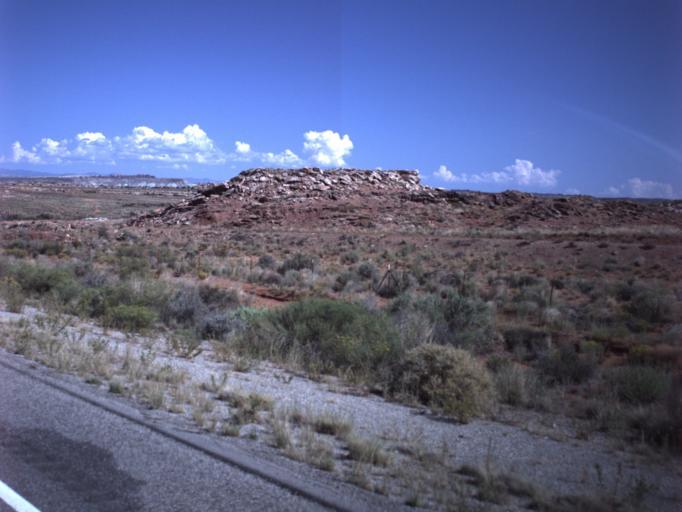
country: US
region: Utah
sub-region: Grand County
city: Moab
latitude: 38.6668
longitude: -109.6829
